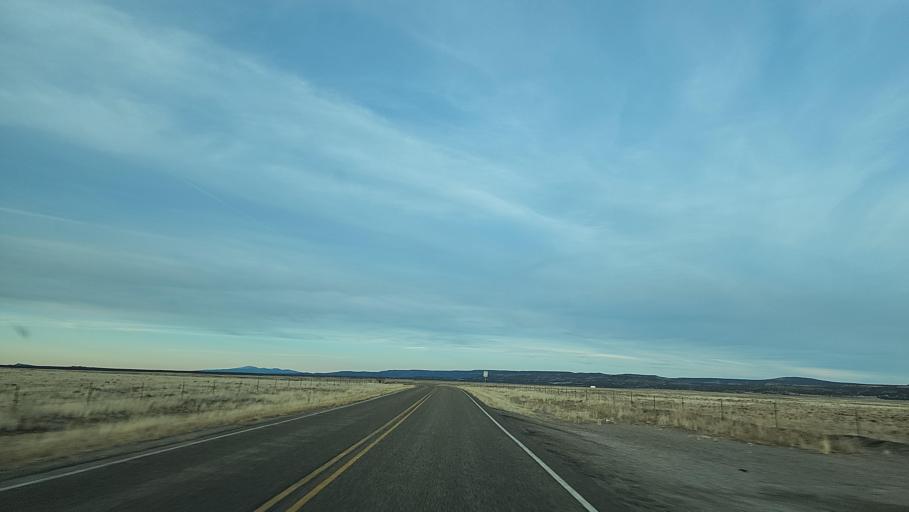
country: US
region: New Mexico
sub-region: Cibola County
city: Grants
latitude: 34.6912
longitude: -108.0558
